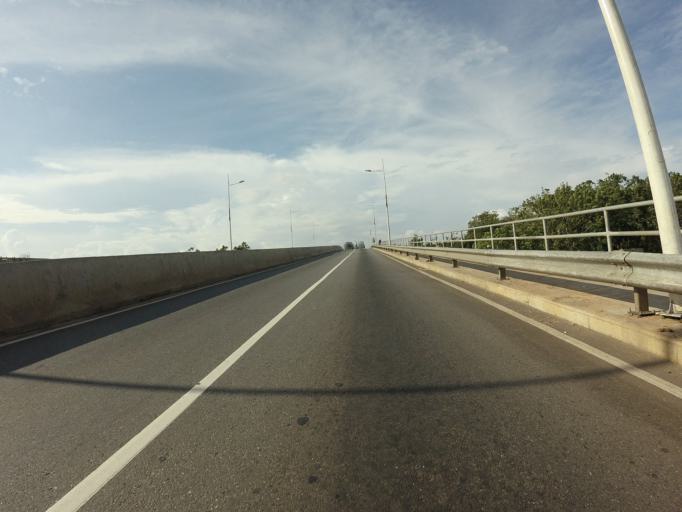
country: GH
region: Greater Accra
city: Medina Estates
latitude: 5.6189
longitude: -0.1526
